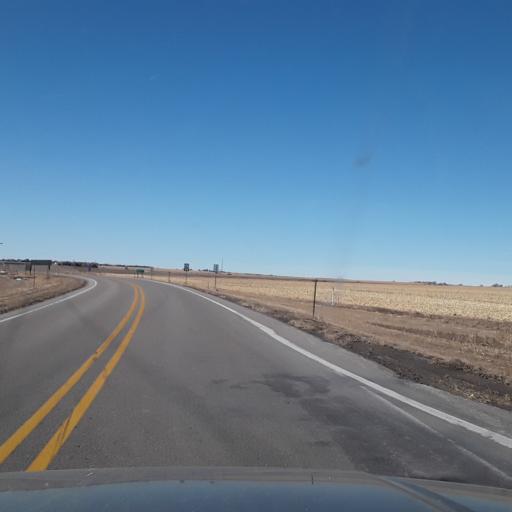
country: US
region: Nebraska
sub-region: Dawson County
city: Gothenburg
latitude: 40.7036
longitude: -100.1685
